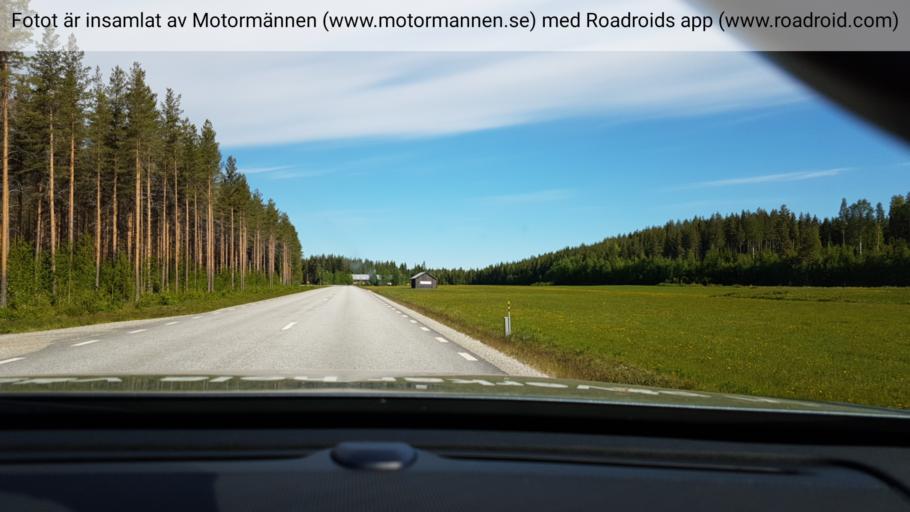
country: SE
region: Vaesterbotten
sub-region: Vindelns Kommun
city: Vindeln
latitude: 64.1982
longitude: 19.4531
